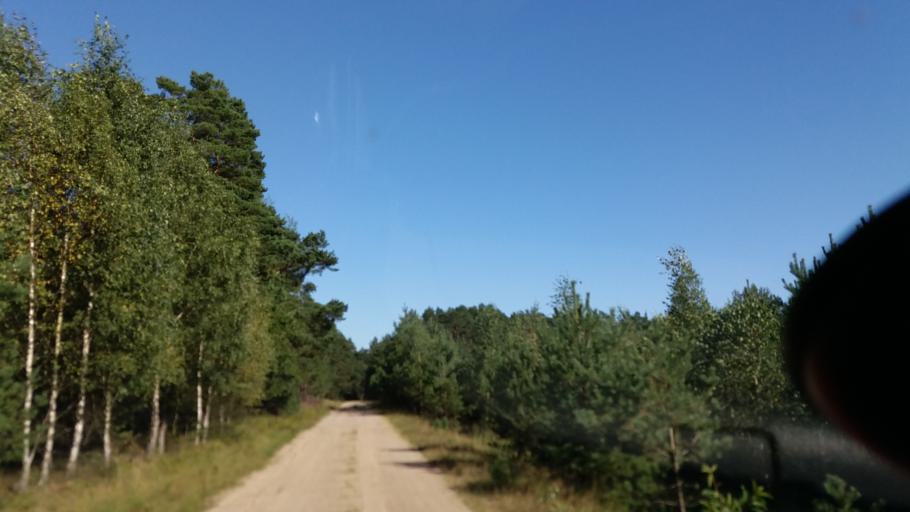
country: PL
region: West Pomeranian Voivodeship
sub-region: Powiat szczecinecki
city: Borne Sulinowo
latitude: 53.5552
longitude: 16.5112
